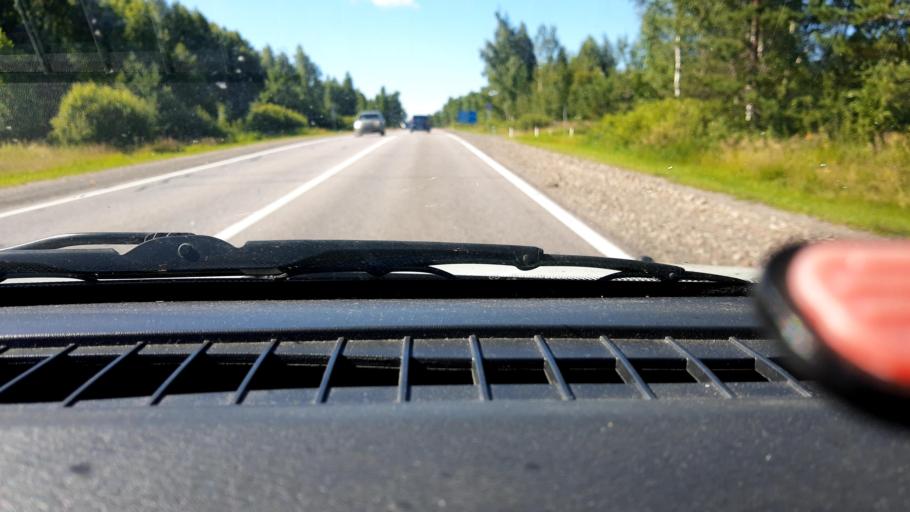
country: RU
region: Nizjnij Novgorod
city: Surovatikha
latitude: 55.7477
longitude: 43.9900
